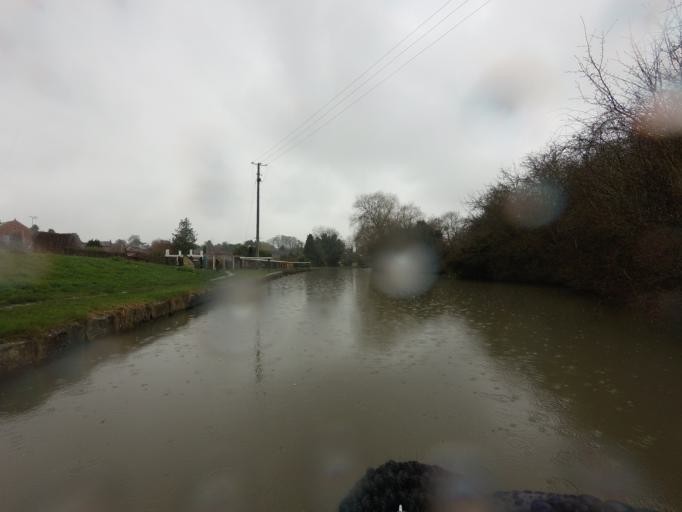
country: GB
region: England
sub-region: Northamptonshire
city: Blisworth
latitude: 52.1772
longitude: -0.9411
